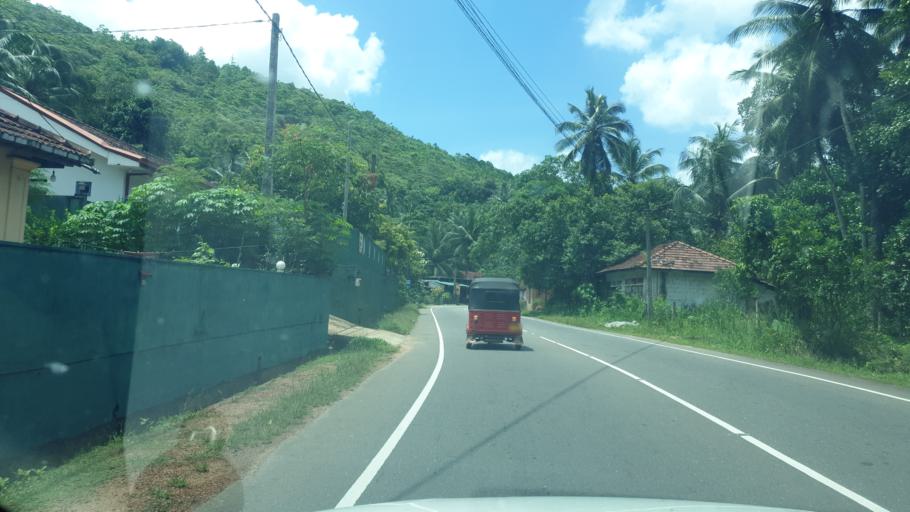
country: LK
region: Western
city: Horawala Junction
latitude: 6.5229
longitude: 80.1951
